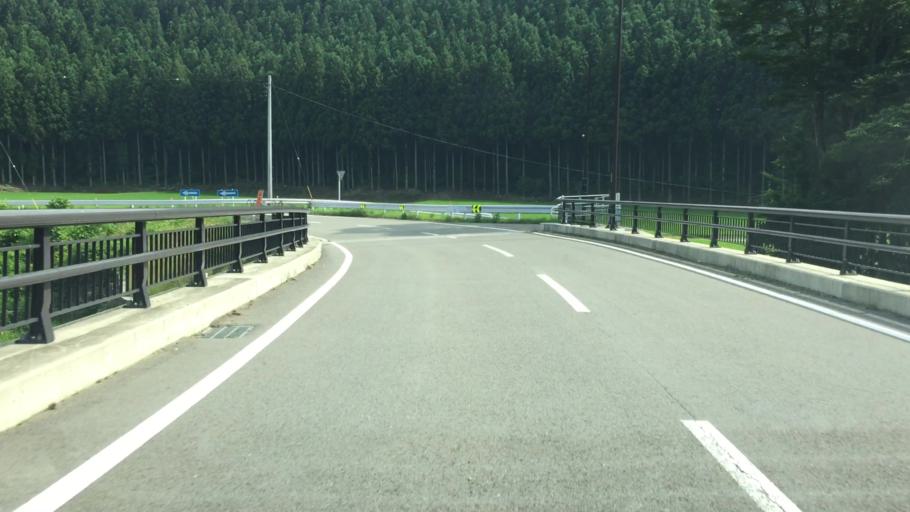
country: JP
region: Tochigi
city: Kuroiso
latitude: 37.0465
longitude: 139.9448
